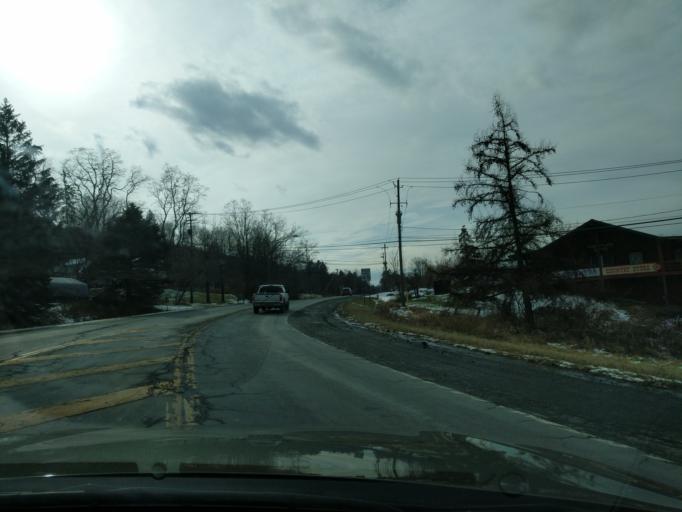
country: US
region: New York
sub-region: Tompkins County
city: Northeast Ithaca
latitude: 42.4683
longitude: -76.4092
